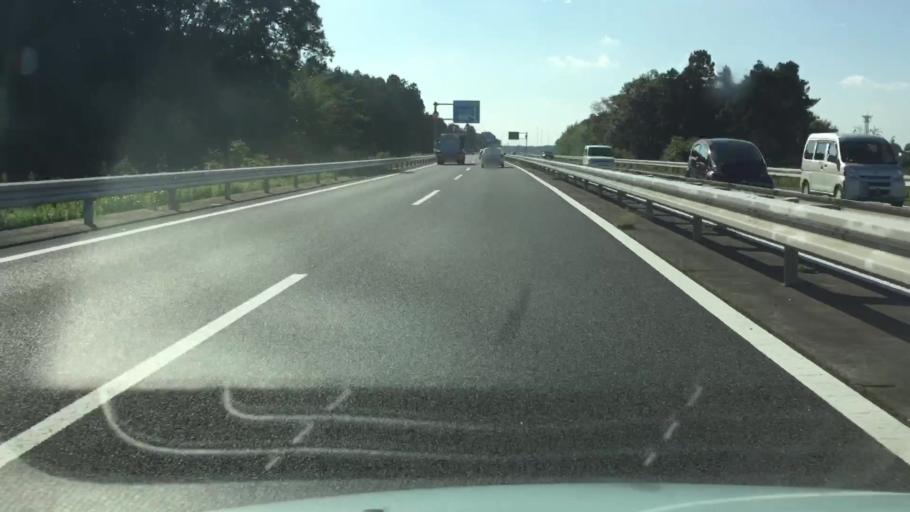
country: JP
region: Tochigi
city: Mooka
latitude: 36.4970
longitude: 139.9901
